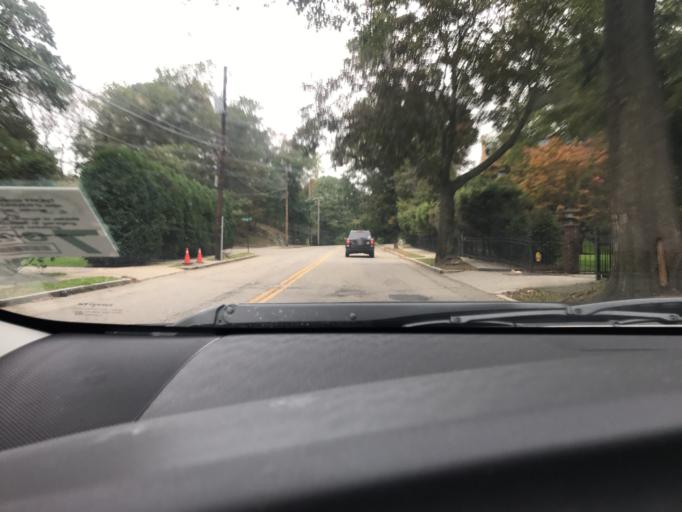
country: US
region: Massachusetts
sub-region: Middlesex County
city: Newton
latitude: 42.3404
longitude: -71.2180
